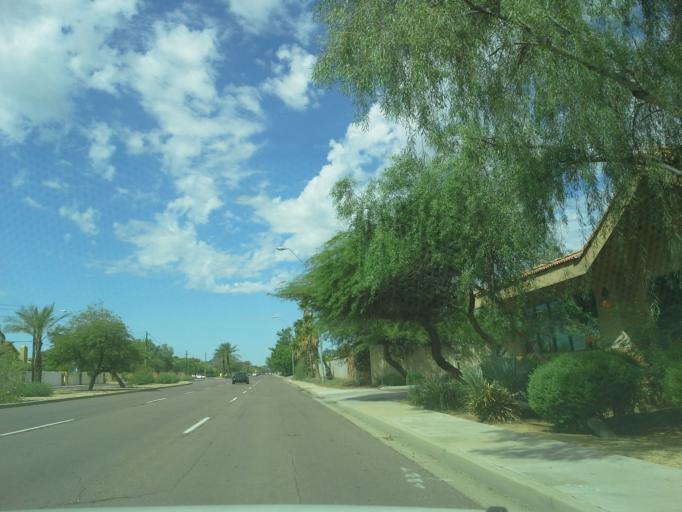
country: US
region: Arizona
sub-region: Maricopa County
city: Paradise Valley
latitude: 33.6262
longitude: -111.9805
